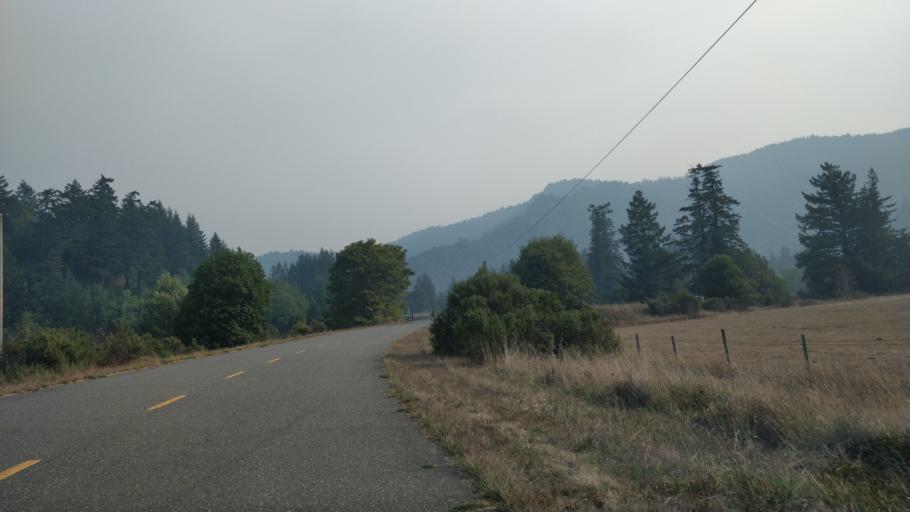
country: US
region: California
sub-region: Humboldt County
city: Rio Dell
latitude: 40.2782
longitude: -124.2439
